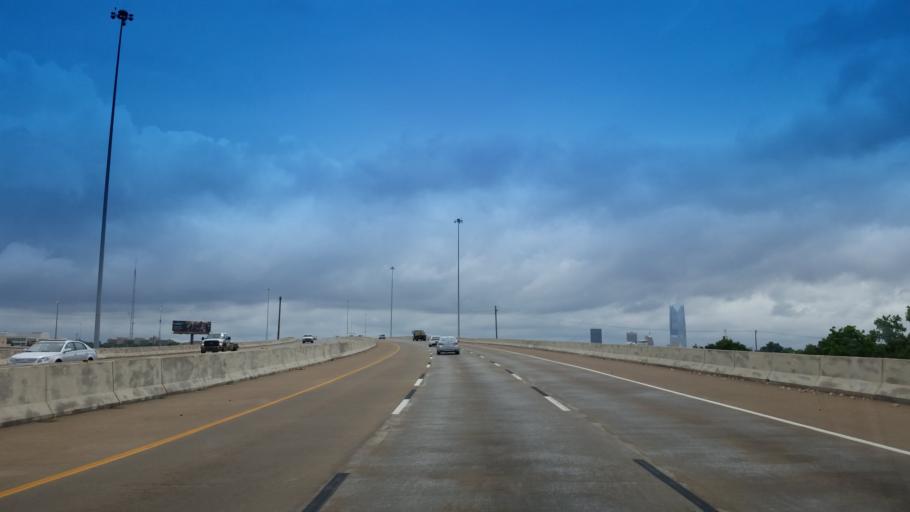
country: US
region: Oklahoma
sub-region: Oklahoma County
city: Oklahoma City
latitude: 35.4964
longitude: -97.5138
